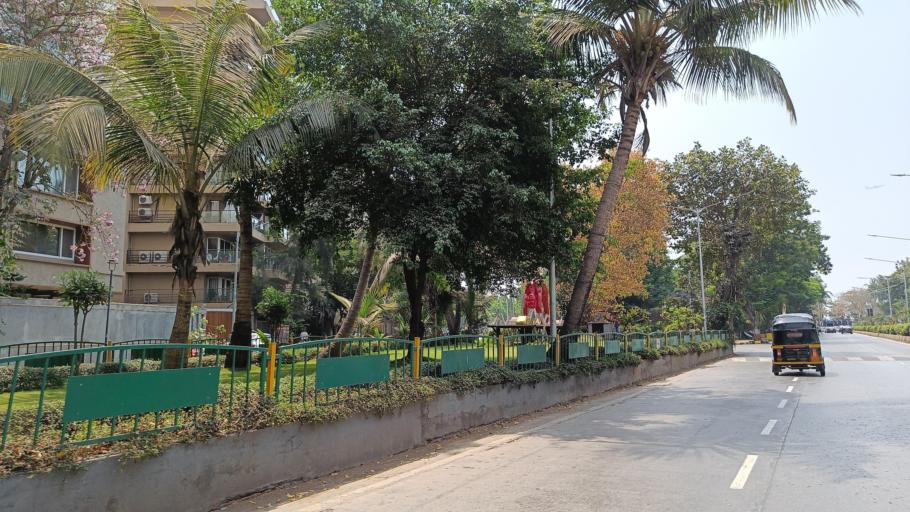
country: IN
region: Maharashtra
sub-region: Mumbai Suburban
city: Mumbai
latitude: 19.1062
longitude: 72.8300
